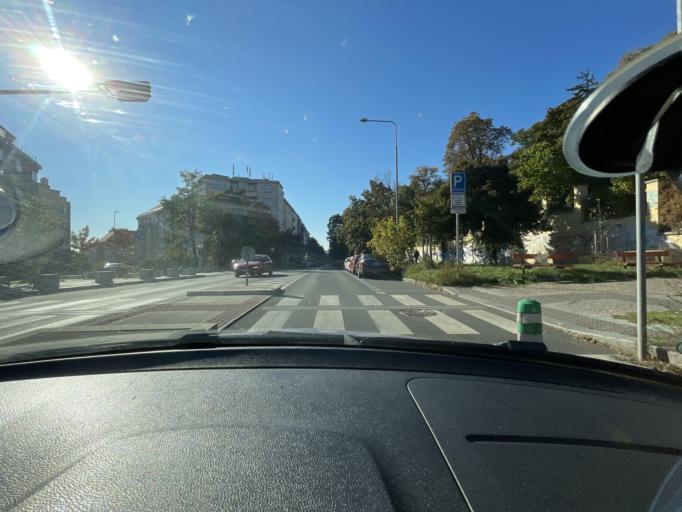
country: CZ
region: Praha
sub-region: Praha 8
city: Karlin
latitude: 50.0727
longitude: 14.4600
